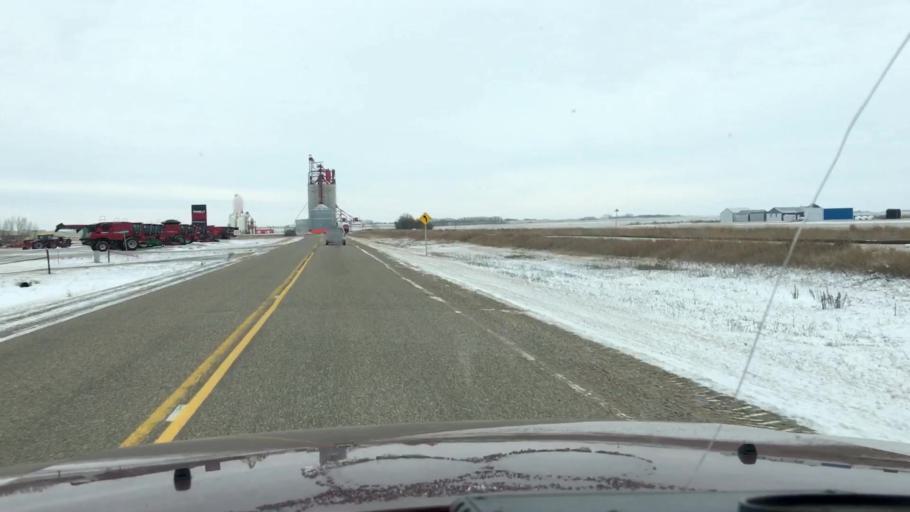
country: CA
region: Saskatchewan
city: Watrous
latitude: 51.2516
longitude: -105.9795
